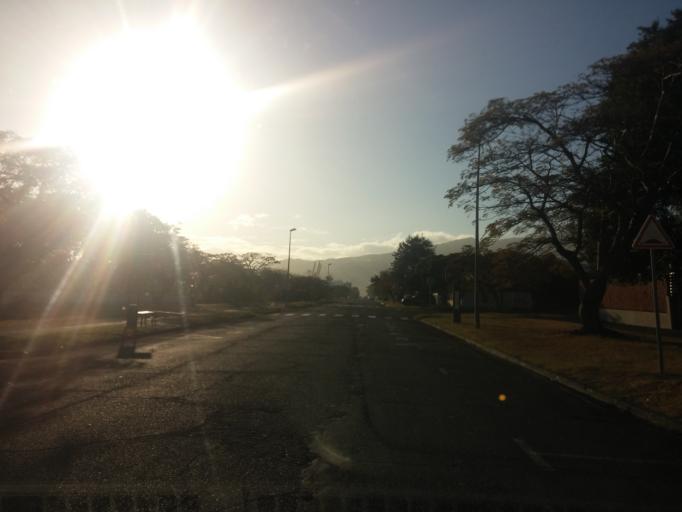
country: RE
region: Reunion
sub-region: Reunion
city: Le Port
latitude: -20.9343
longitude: 55.3031
